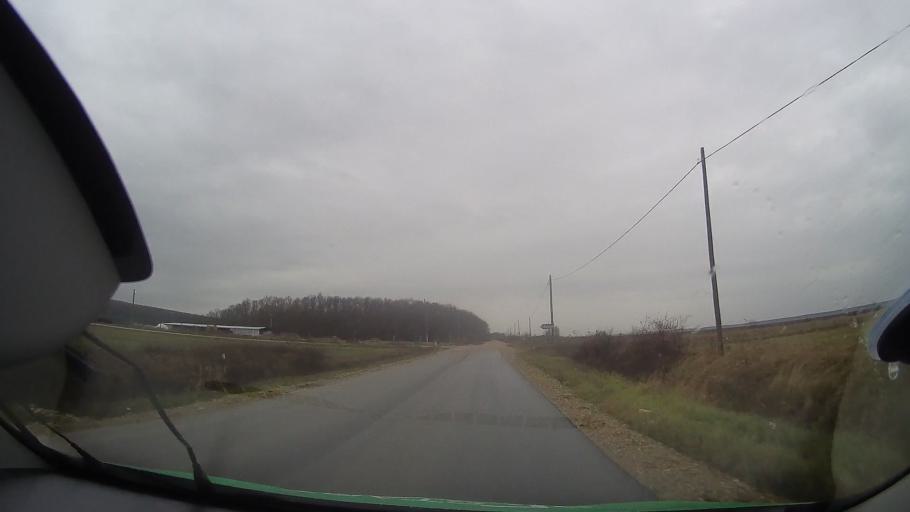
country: RO
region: Bihor
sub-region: Comuna Olcea
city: Olcea
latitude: 46.6898
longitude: 22.0090
